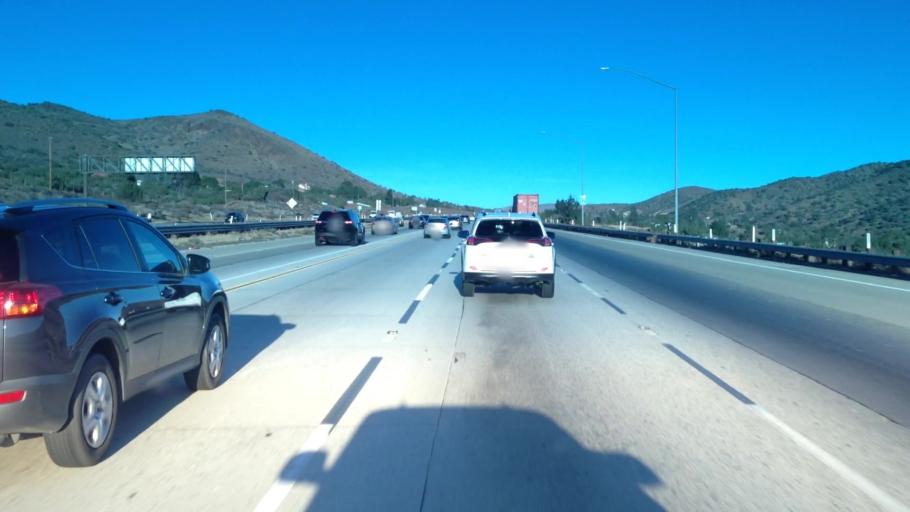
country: US
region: California
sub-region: Los Angeles County
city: Agua Dulce
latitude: 34.4931
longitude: -118.2803
